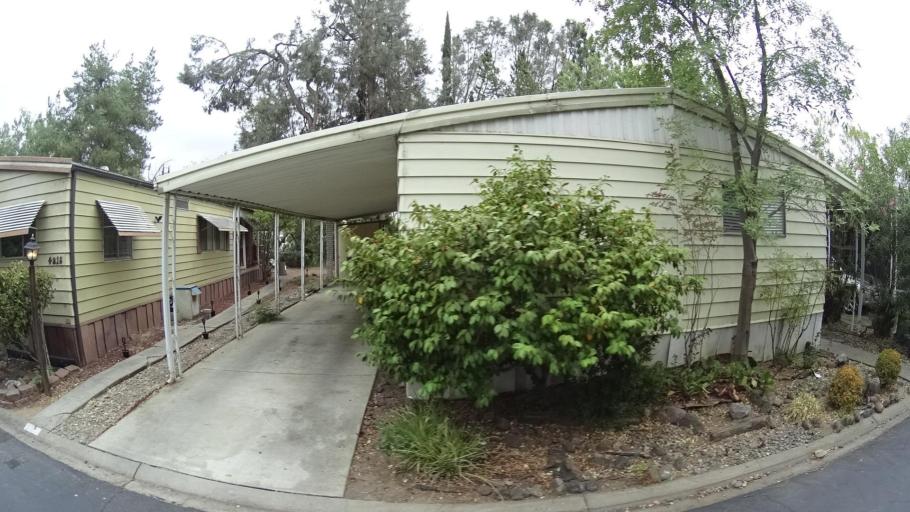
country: US
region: California
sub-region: Placer County
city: Rocklin
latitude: 38.7864
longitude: -121.2292
